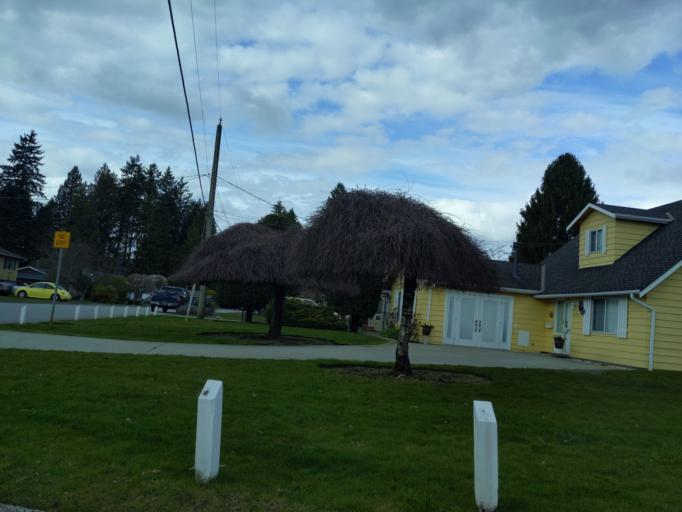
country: CA
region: British Columbia
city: Pitt Meadows
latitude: 49.2153
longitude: -122.6815
